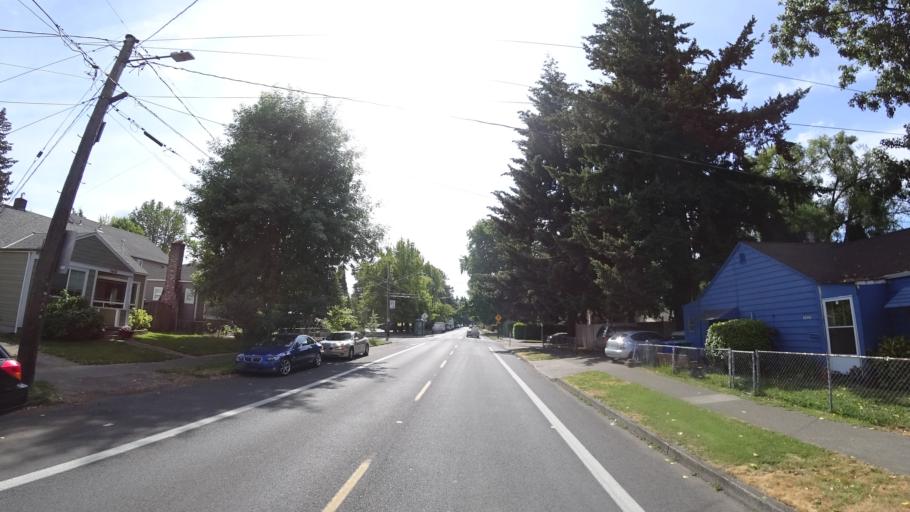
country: US
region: Washington
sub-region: Clark County
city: Vancouver
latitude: 45.5912
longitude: -122.7225
